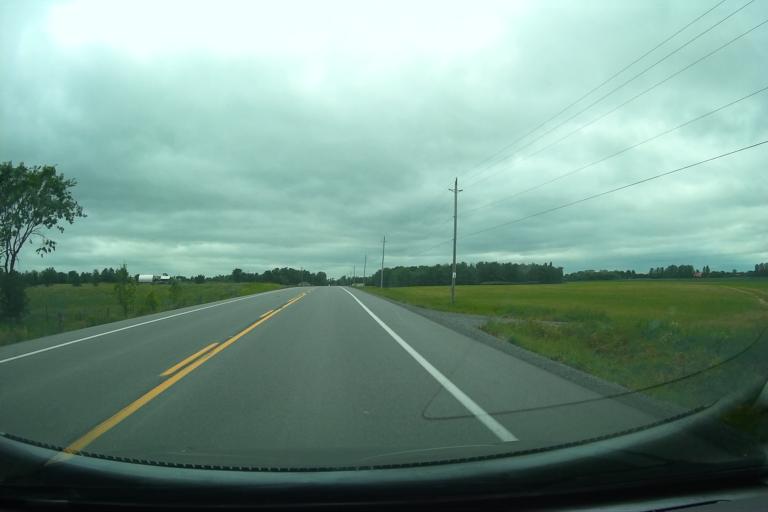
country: CA
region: Ontario
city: Carleton Place
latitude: 45.1425
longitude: -75.9643
